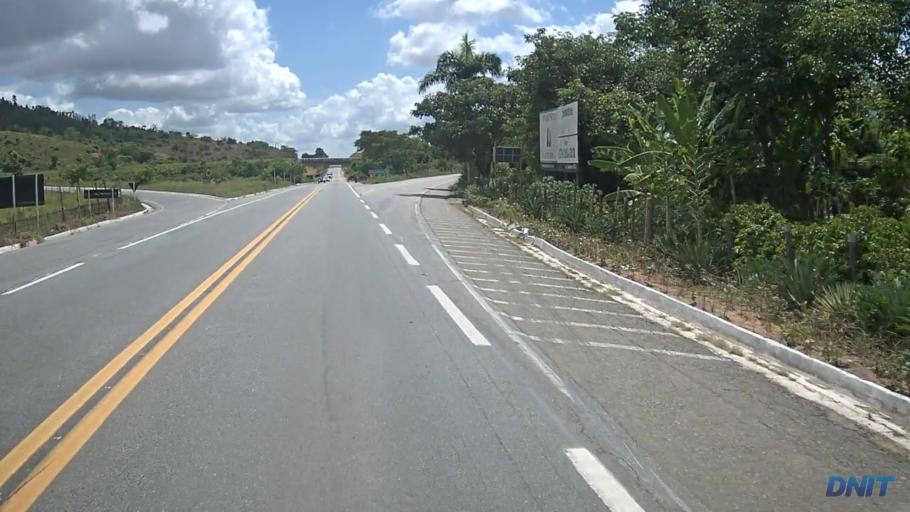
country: BR
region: Minas Gerais
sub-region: Governador Valadares
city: Governador Valadares
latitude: -18.9155
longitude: -42.0114
